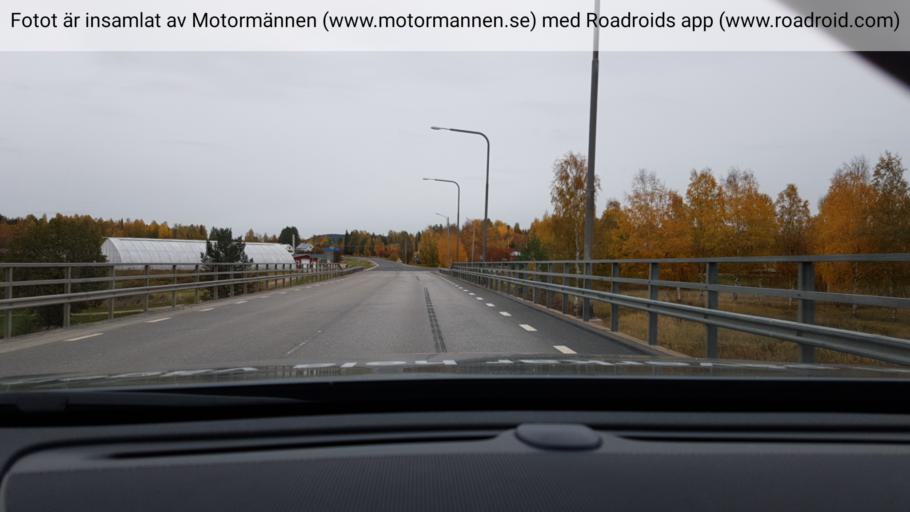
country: SE
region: Norrbotten
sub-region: Overkalix Kommun
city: OEverkalix
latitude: 66.3640
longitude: 22.8415
